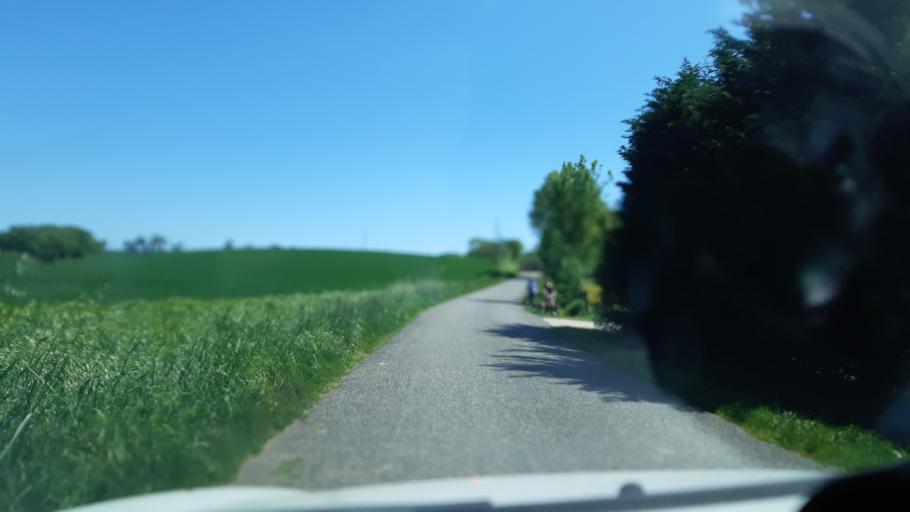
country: FR
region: Midi-Pyrenees
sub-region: Departement du Gers
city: Samatan
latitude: 43.5222
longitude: 0.9893
